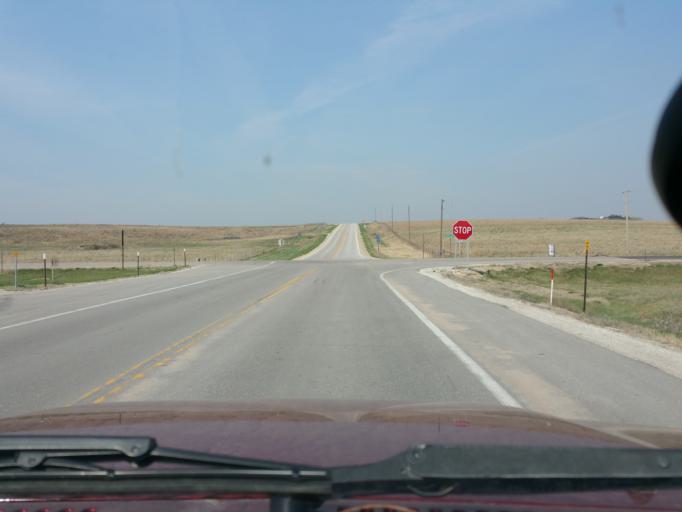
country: US
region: Kansas
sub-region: Marshall County
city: Blue Rapids
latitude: 39.4363
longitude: -96.7635
